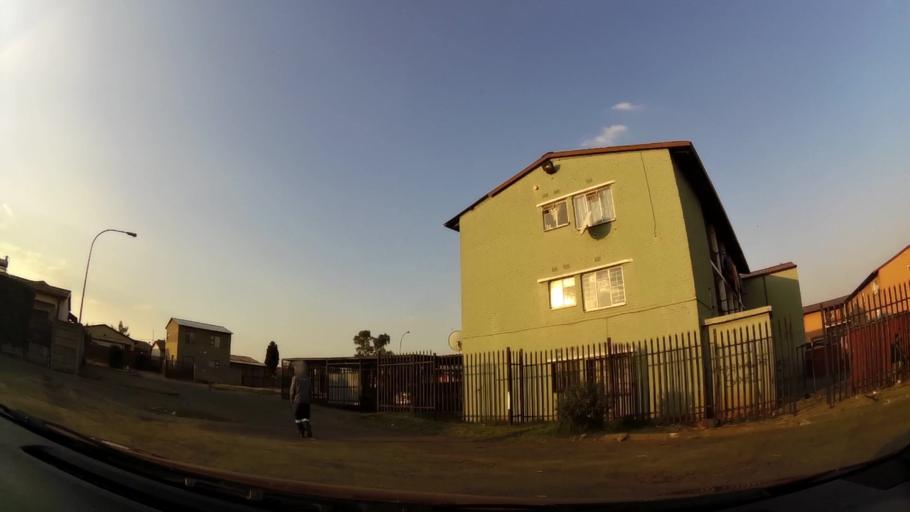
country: ZA
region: Gauteng
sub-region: City of Johannesburg Metropolitan Municipality
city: Soweto
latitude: -26.2828
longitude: 27.9070
